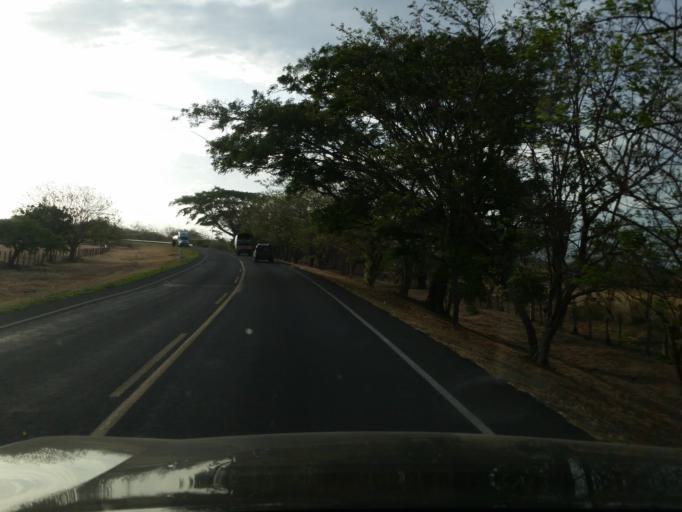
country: NI
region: Rivas
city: Belen
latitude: 11.5973
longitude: -85.9132
